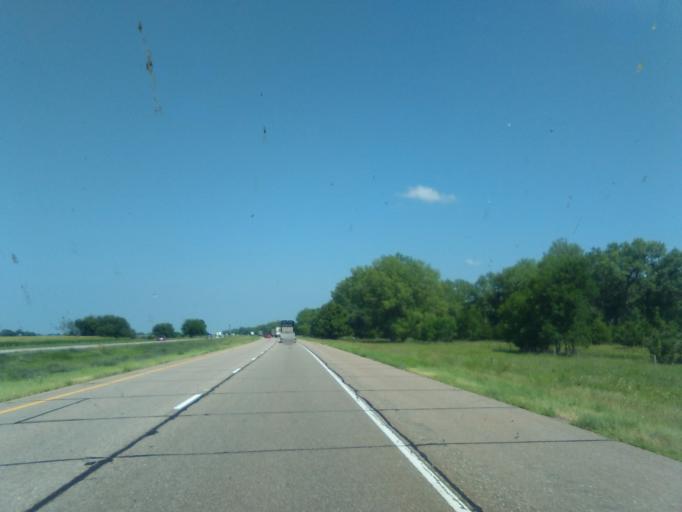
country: US
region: Nebraska
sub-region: Buffalo County
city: Kearney
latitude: 40.6725
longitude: -99.2214
